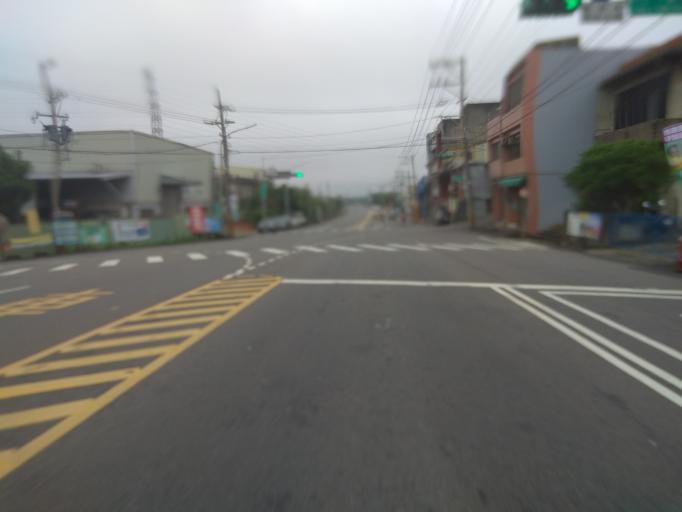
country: TW
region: Taiwan
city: Taoyuan City
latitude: 25.0185
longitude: 121.1240
